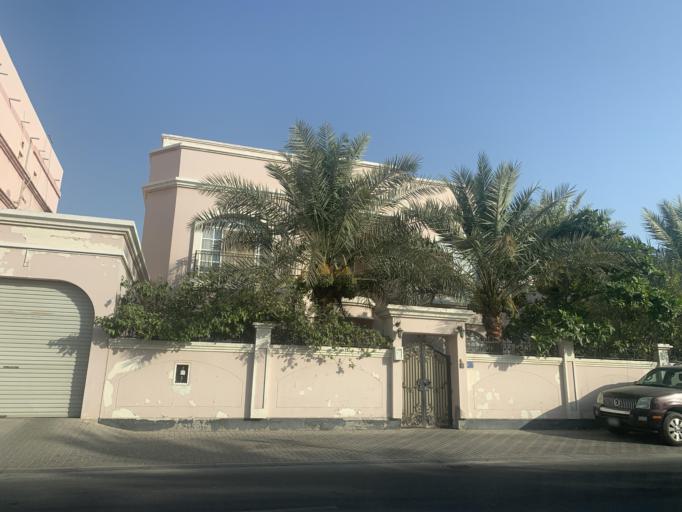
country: BH
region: Manama
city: Jidd Hafs
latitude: 26.2096
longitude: 50.5315
